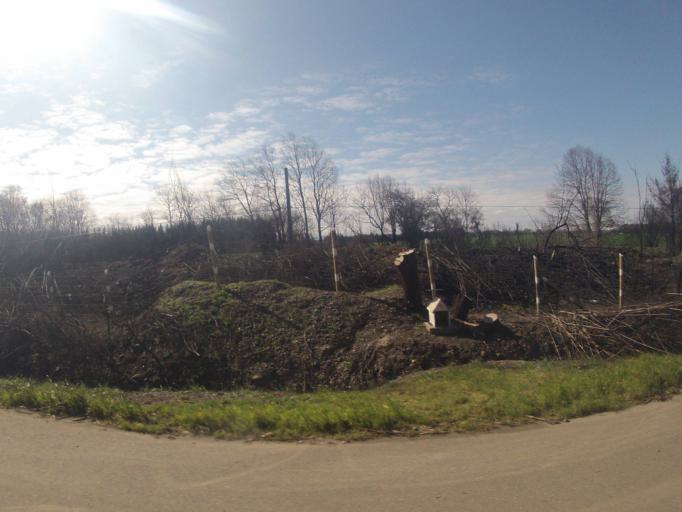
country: CL
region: Araucania
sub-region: Provincia de Malleco
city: Victoria
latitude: -38.1527
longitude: -72.3065
